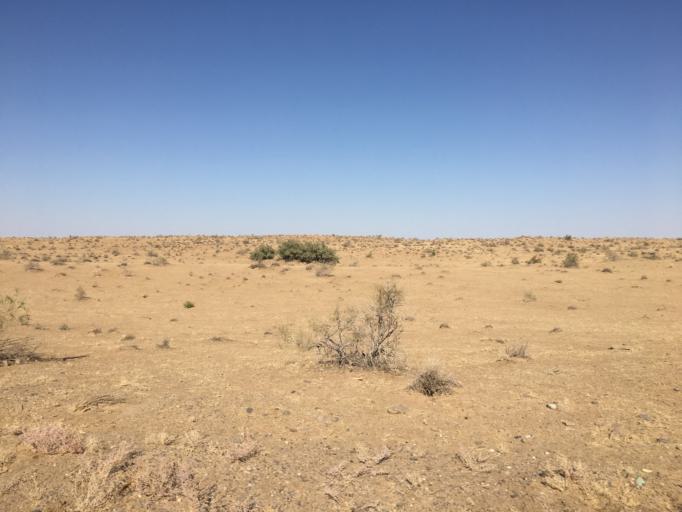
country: IR
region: Razavi Khorasan
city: Sarakhs
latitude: 36.7658
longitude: 61.3239
